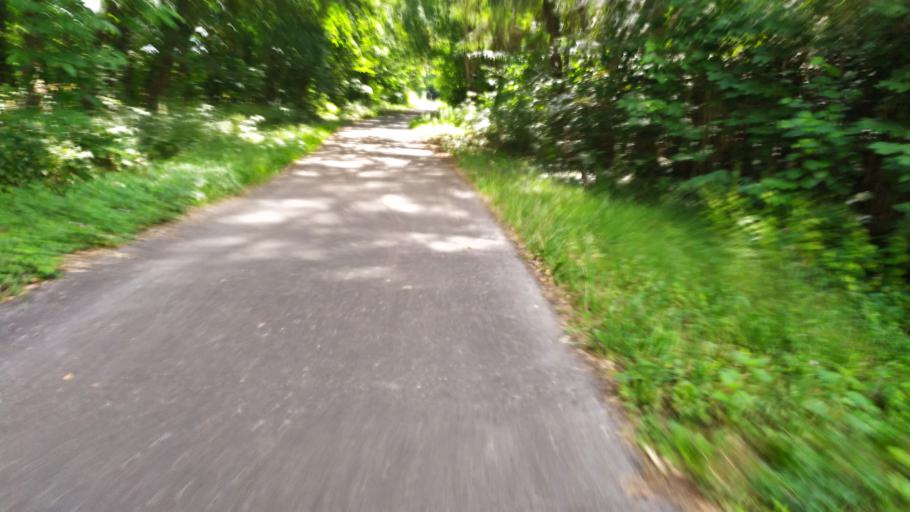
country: BE
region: Wallonia
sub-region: Province de Namur
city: Houyet
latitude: 50.1620
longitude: 5.0623
